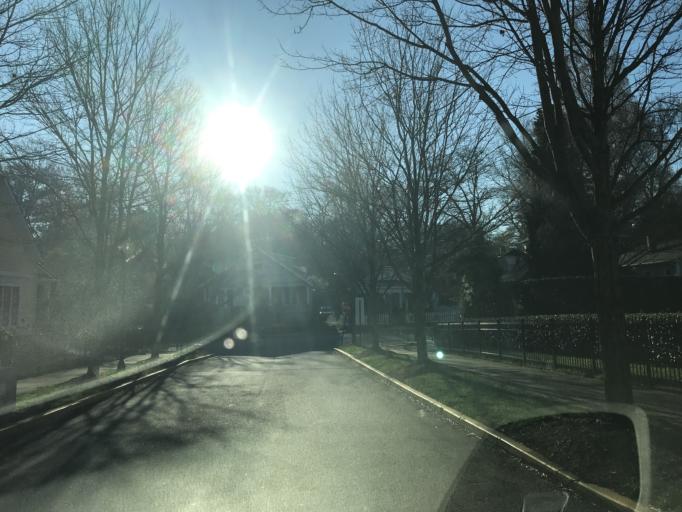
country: US
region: Georgia
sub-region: Fulton County
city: Atlanta
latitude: 33.7593
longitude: -84.3614
